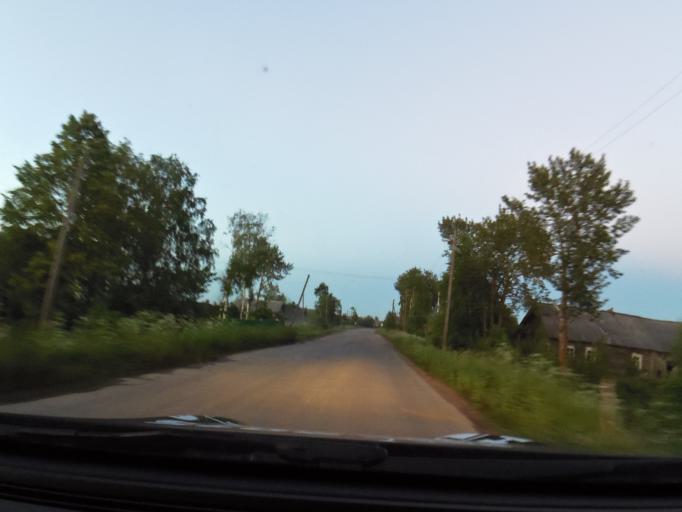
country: RU
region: Vologda
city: Vytegra
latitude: 60.9949
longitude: 36.3392
